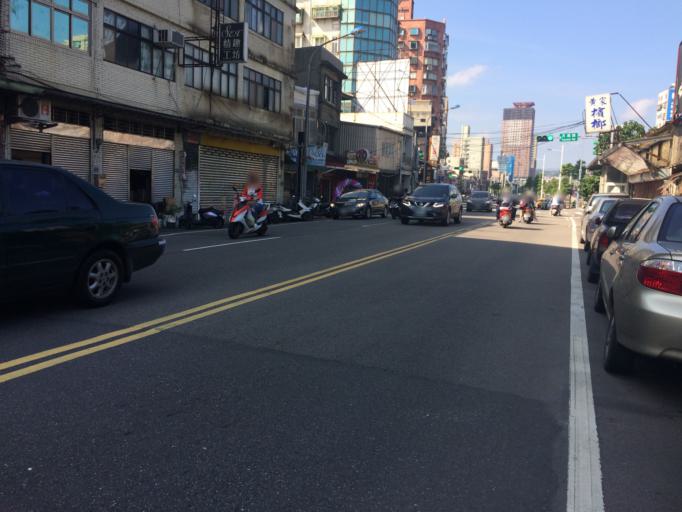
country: TW
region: Taiwan
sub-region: Keelung
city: Keelung
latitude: 25.1282
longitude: 121.7568
